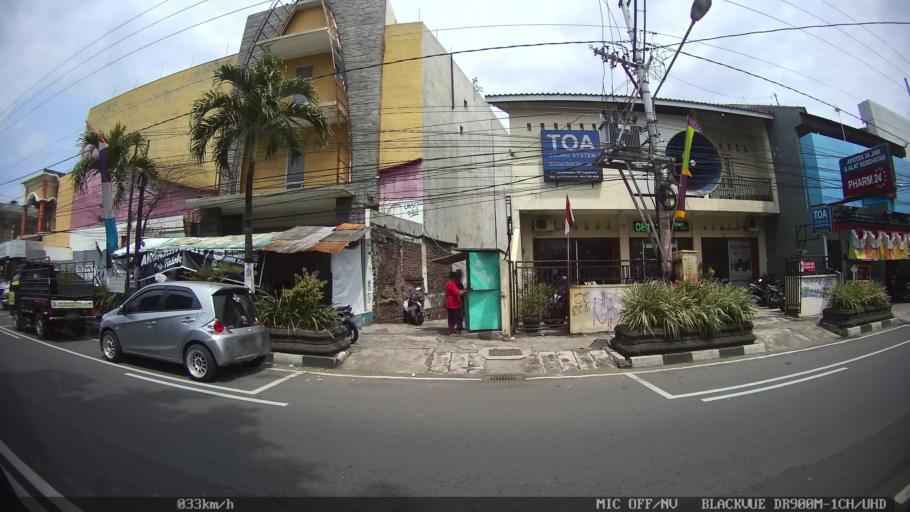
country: ID
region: Daerah Istimewa Yogyakarta
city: Yogyakarta
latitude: -7.8030
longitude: 110.3898
